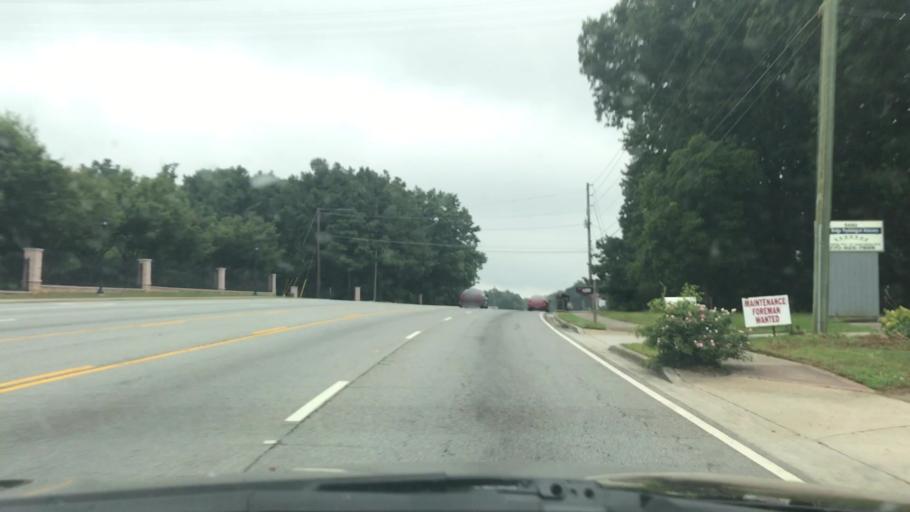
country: US
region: Georgia
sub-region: Gwinnett County
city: Lilburn
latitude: 33.8840
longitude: -84.1607
